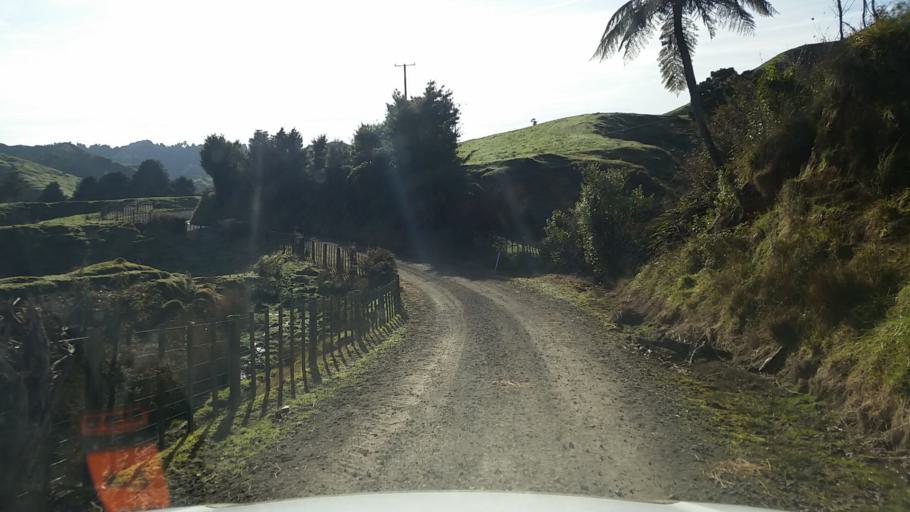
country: NZ
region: Taranaki
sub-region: South Taranaki District
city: Eltham
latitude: -39.3155
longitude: 174.5337
